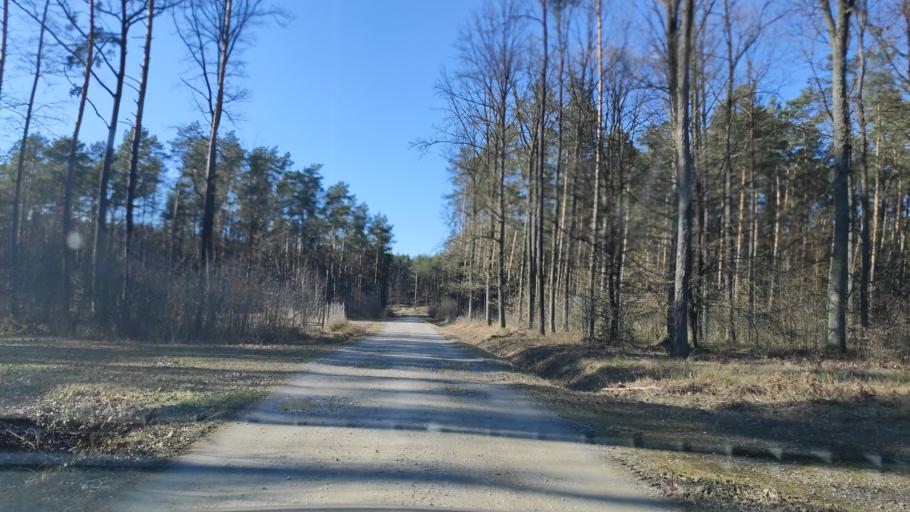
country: PL
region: Masovian Voivodeship
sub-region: Powiat radomski
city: Jedlnia-Letnisko
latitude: 51.4728
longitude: 21.2991
